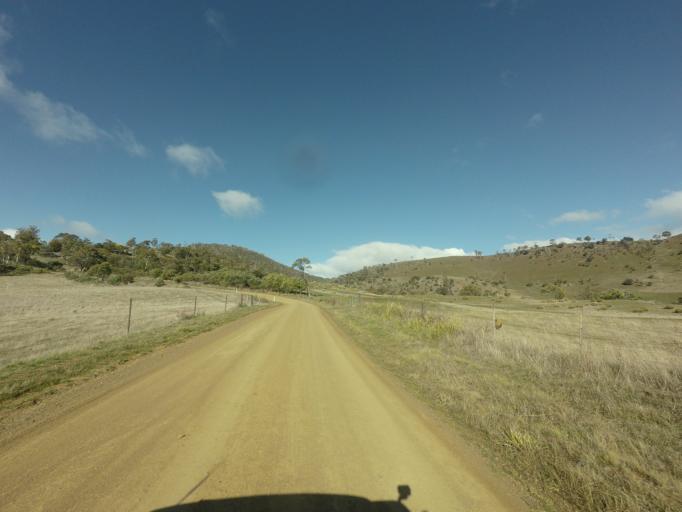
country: AU
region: Tasmania
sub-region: Derwent Valley
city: New Norfolk
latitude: -42.7038
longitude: 146.9944
